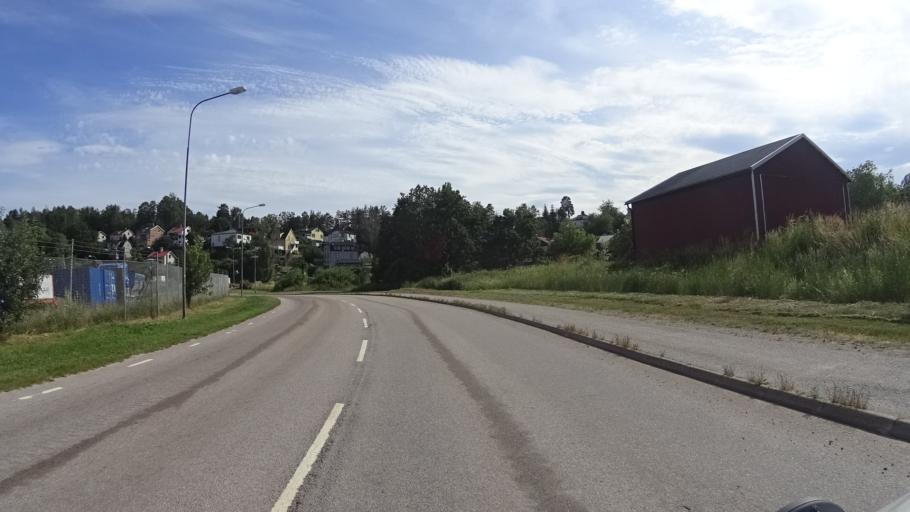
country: SE
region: Kalmar
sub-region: Vasterviks Kommun
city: Gamleby
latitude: 57.8978
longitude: 16.4101
